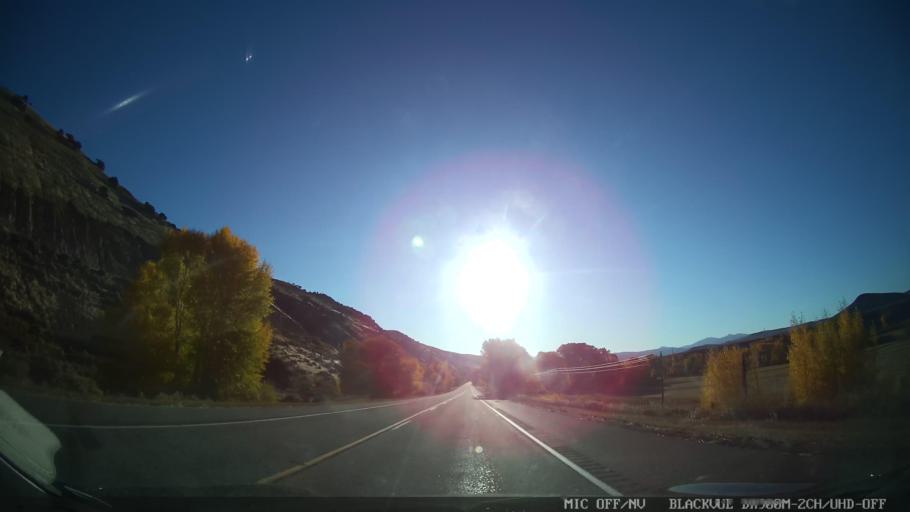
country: US
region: Colorado
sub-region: Grand County
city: Hot Sulphur Springs
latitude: 40.0659
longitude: -106.1977
